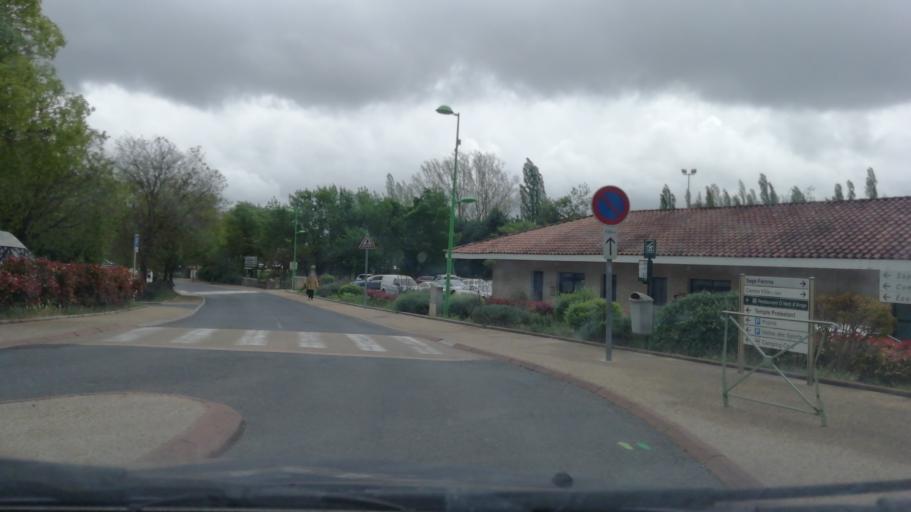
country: FR
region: Languedoc-Roussillon
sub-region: Departement de l'Herault
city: Saint-Martin-de-Londres
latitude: 43.7927
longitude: 3.7334
